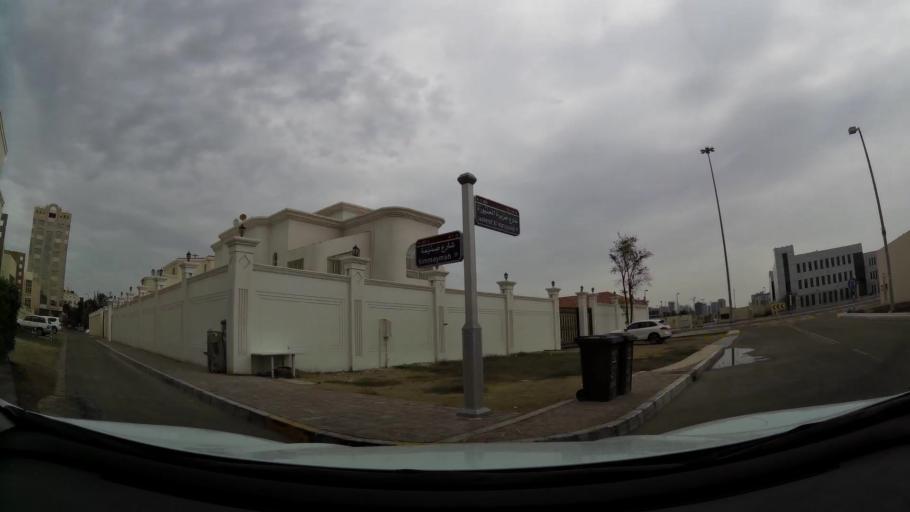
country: AE
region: Abu Dhabi
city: Abu Dhabi
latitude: 24.4360
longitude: 54.4144
